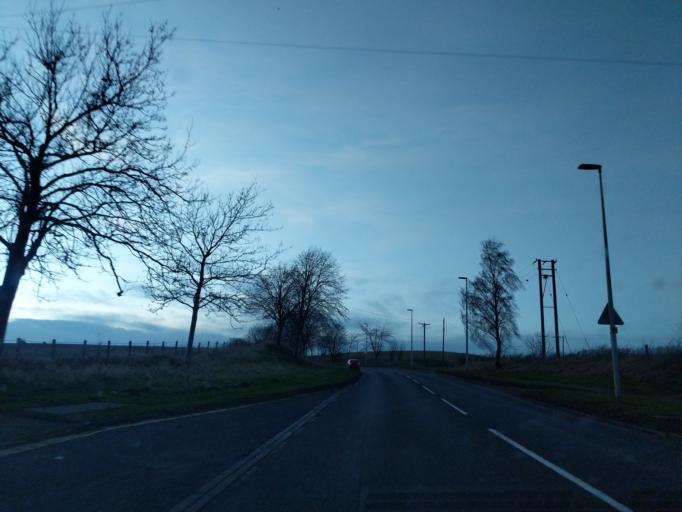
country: GB
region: Scotland
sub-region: Midlothian
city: Bonnyrigg
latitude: 55.8812
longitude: -3.1288
